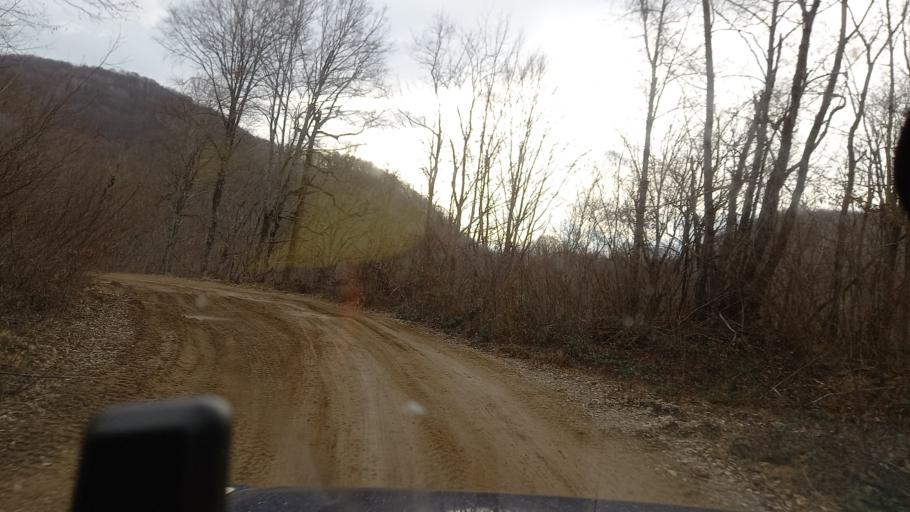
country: RU
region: Adygeya
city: Kamennomostskiy
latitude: 44.1777
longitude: 40.2974
